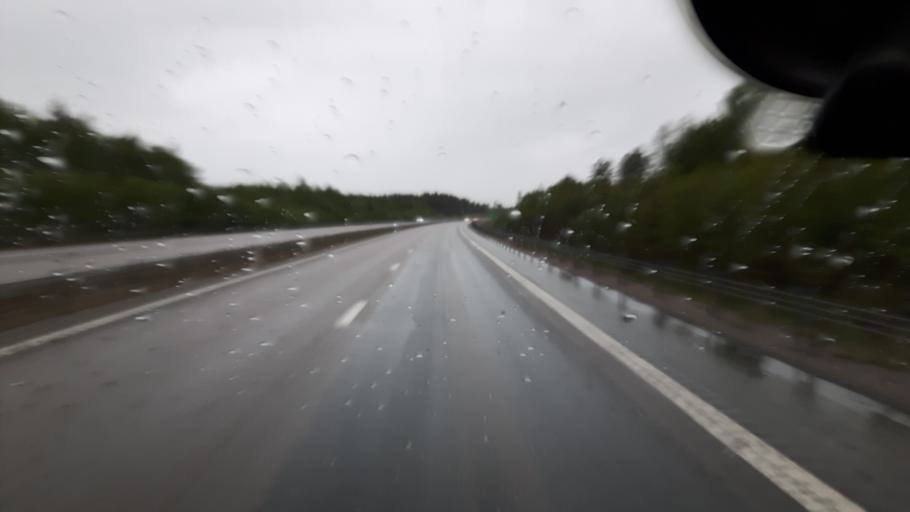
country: SE
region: Uppsala
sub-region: Osthammars Kommun
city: Bjorklinge
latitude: 60.1769
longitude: 17.5097
